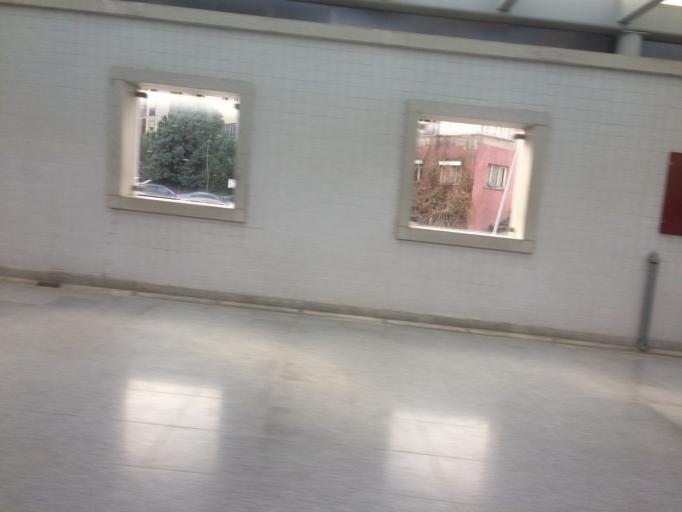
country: TR
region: Izmir
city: Karsiyaka
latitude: 38.4749
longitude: 27.0898
